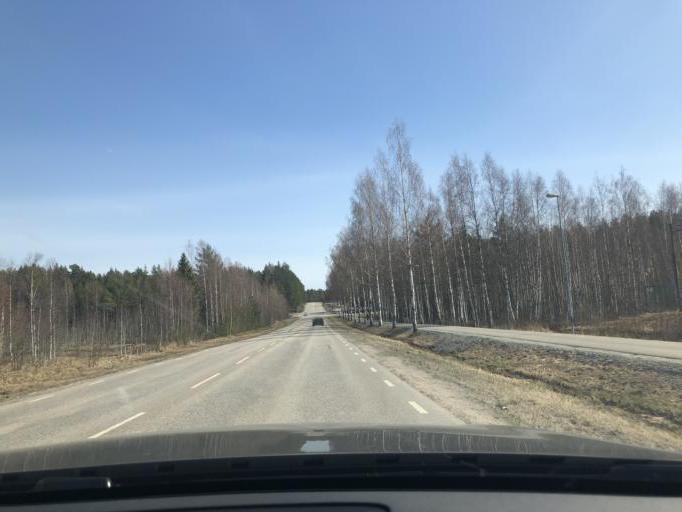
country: SE
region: Gaevleborg
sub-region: Hudiksvalls Kommun
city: Hudiksvall
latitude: 61.7248
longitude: 17.1554
